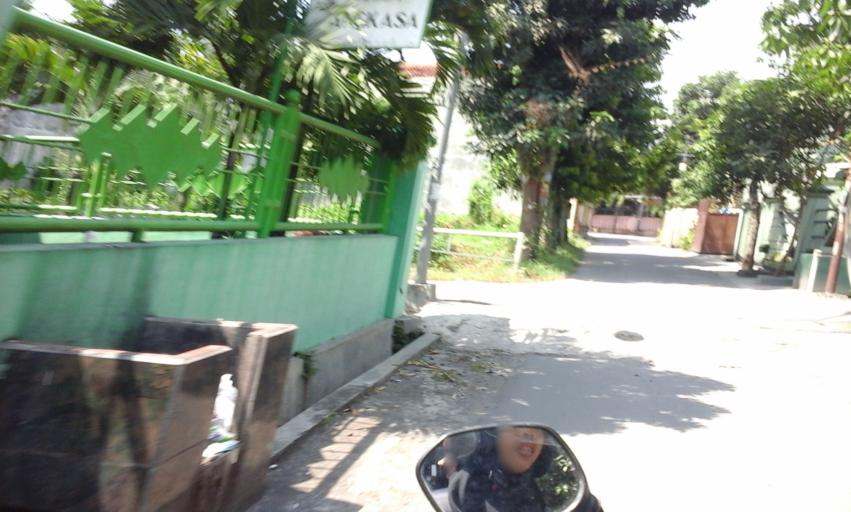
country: ID
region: East Java
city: Sumbersari Wetan
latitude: -8.1709
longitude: 113.7134
